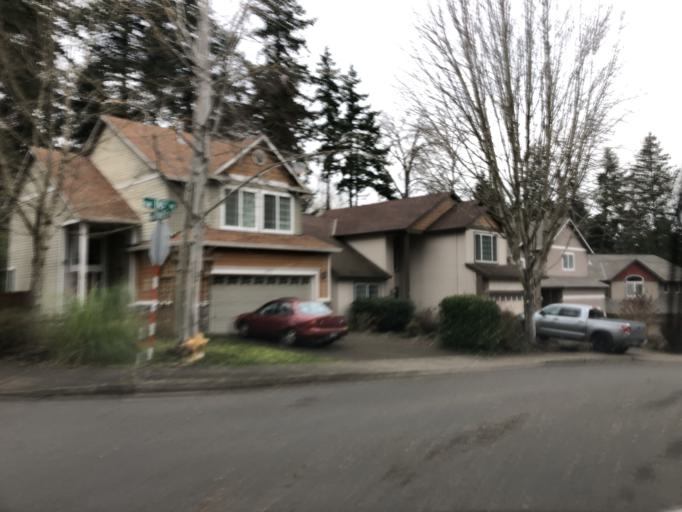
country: US
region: Oregon
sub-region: Washington County
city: King City
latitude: 45.4260
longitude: -122.7964
